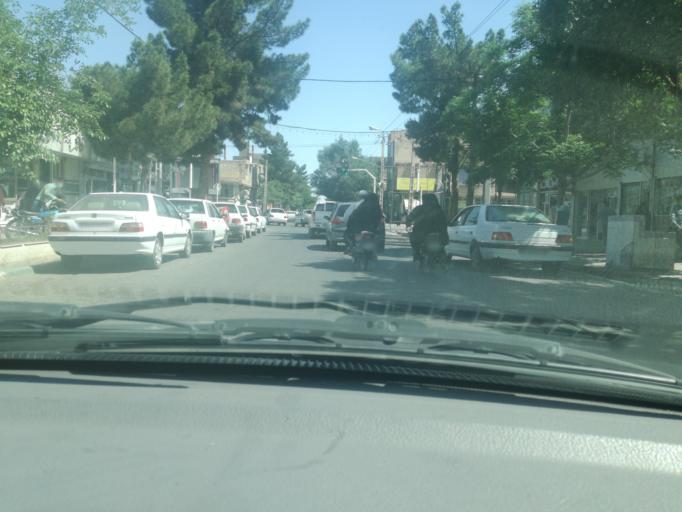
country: IR
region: Razavi Khorasan
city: Sarakhs
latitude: 36.5363
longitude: 61.1632
